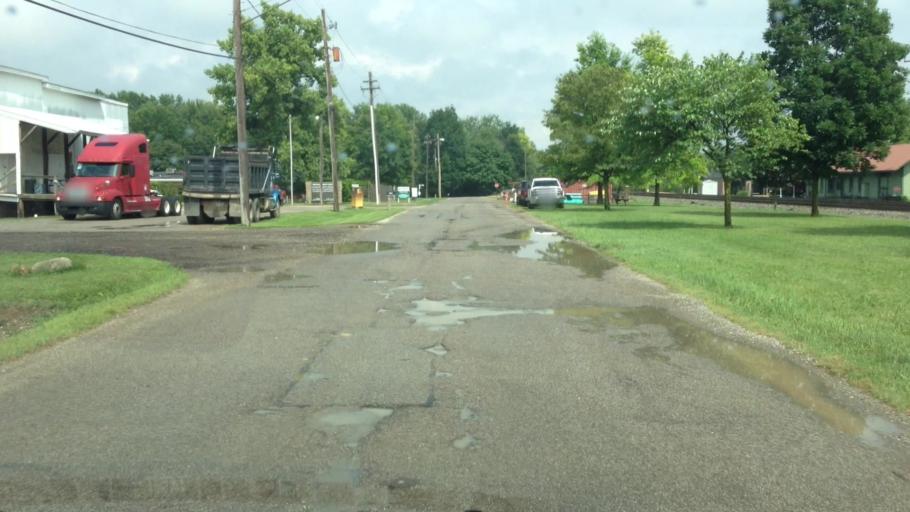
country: US
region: Ohio
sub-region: Cuyahoga County
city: Olmsted Falls
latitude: 41.3755
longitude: -81.9074
